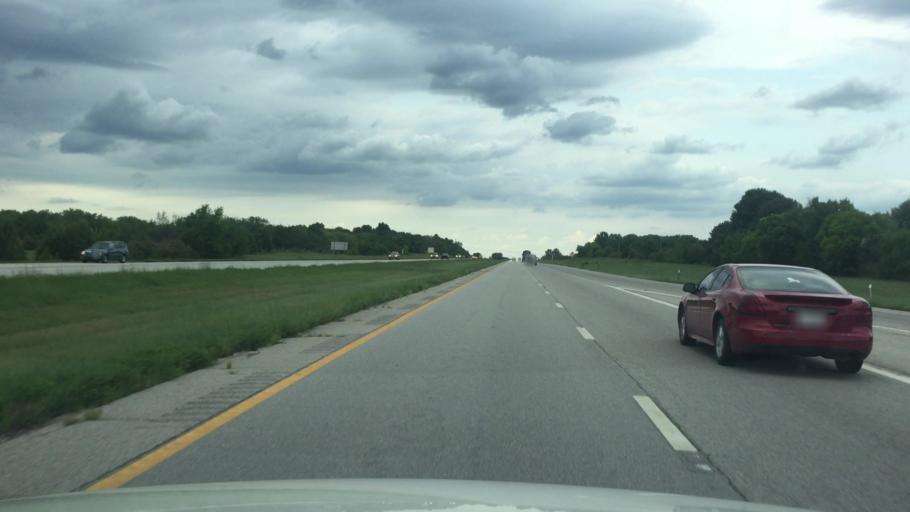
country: US
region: Kansas
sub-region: Miami County
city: Louisburg
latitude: 38.7690
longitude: -94.6776
